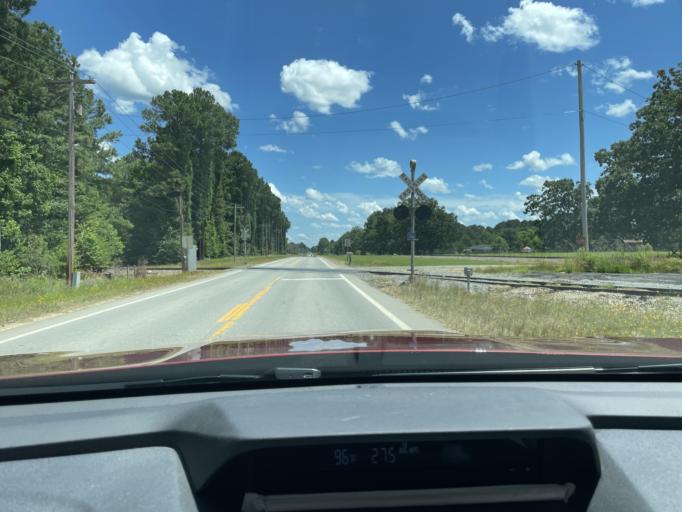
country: US
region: Arkansas
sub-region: Drew County
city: Monticello
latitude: 33.6245
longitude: -91.7527
